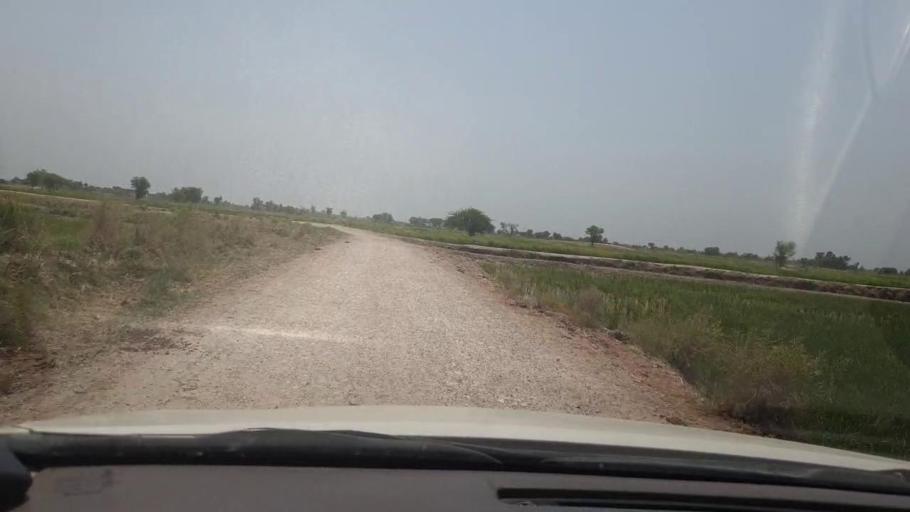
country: PK
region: Sindh
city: Garhi Yasin
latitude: 27.9180
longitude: 68.5545
